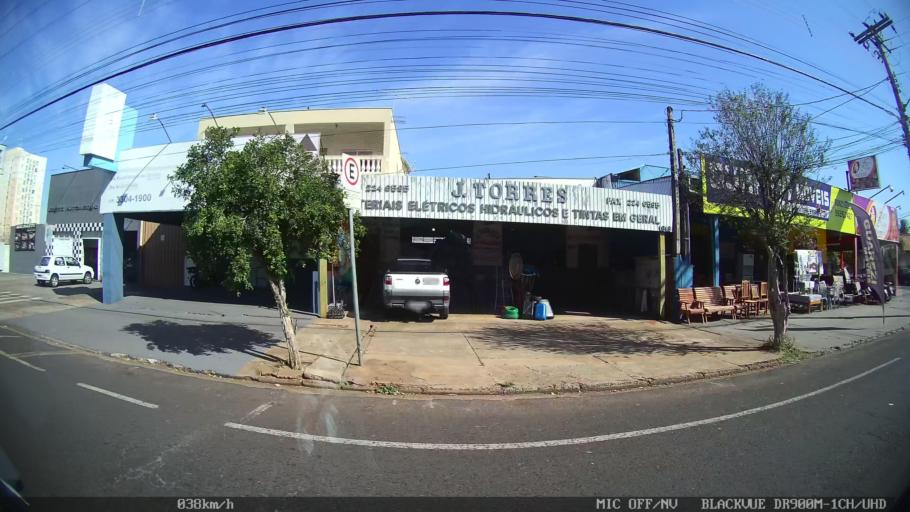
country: BR
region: Sao Paulo
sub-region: Sao Jose Do Rio Preto
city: Sao Jose do Rio Preto
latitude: -20.7837
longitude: -49.3686
